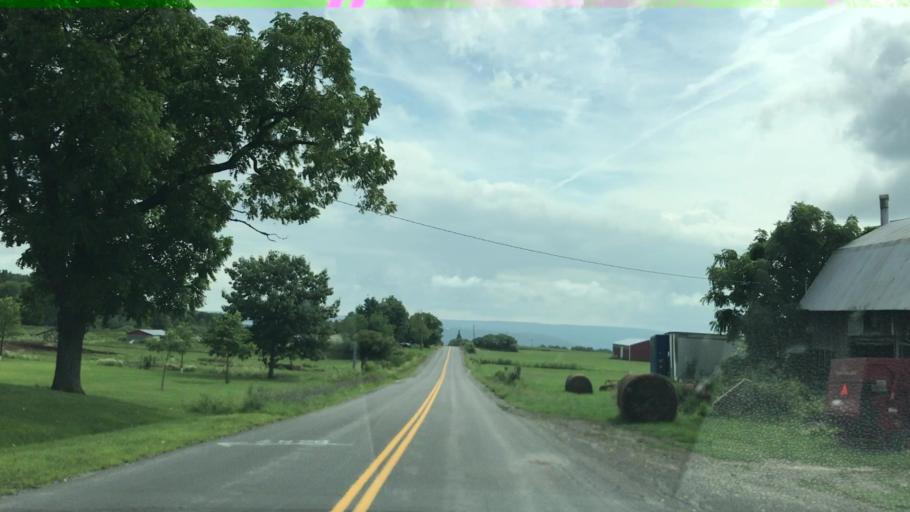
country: US
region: New York
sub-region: Steuben County
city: Sylvan Beach
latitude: 42.5119
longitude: -77.2088
